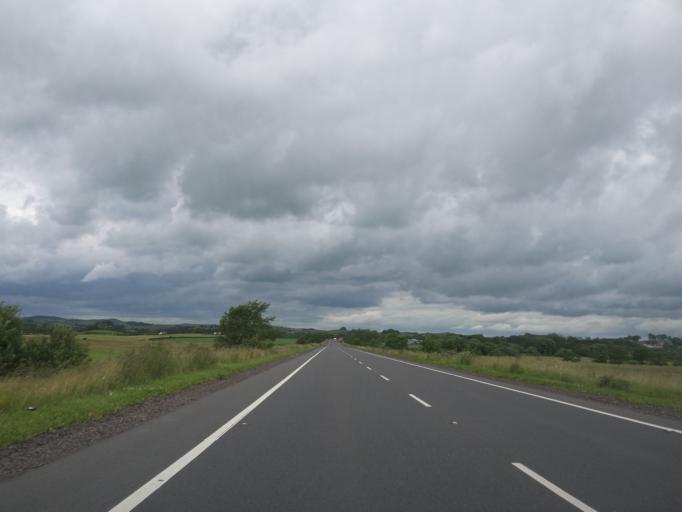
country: GB
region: Scotland
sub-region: Dumfries and Galloway
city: Castle Douglas
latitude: 54.9339
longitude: -3.9489
